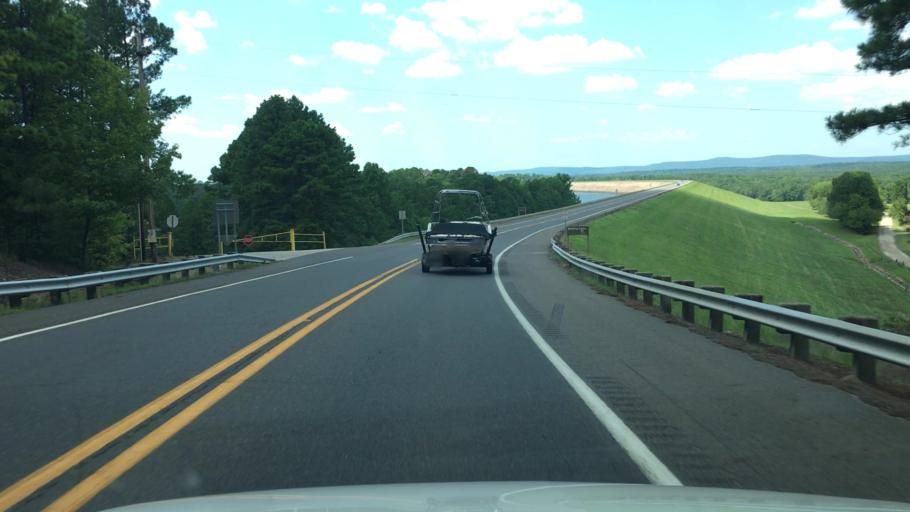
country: US
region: Arkansas
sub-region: Clark County
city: Arkadelphia
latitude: 34.2324
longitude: -93.0997
